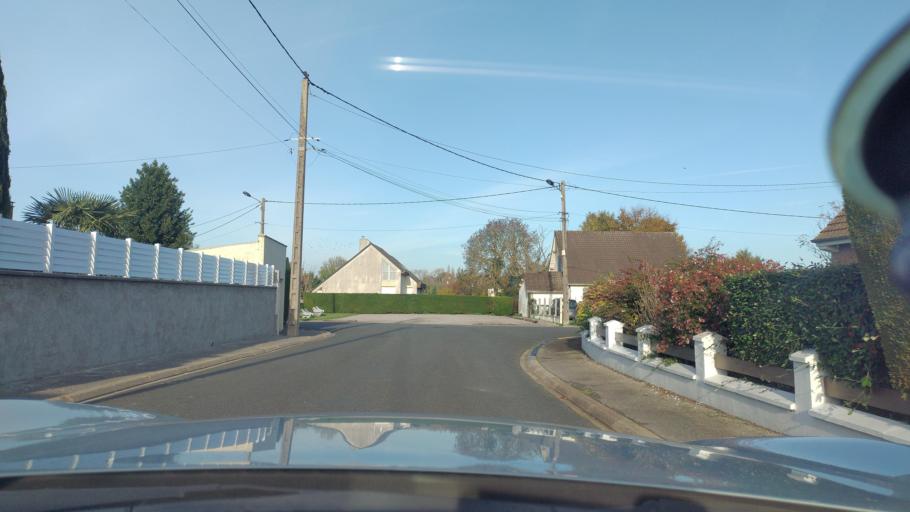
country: FR
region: Picardie
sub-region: Departement de la Somme
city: Fressenneville
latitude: 50.0655
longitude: 1.5771
